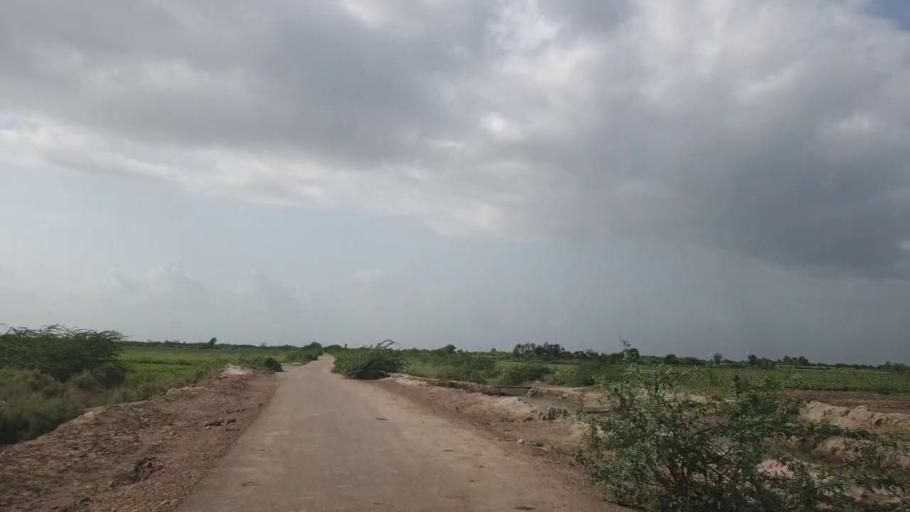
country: PK
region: Sindh
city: Kadhan
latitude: 24.5718
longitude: 69.0613
